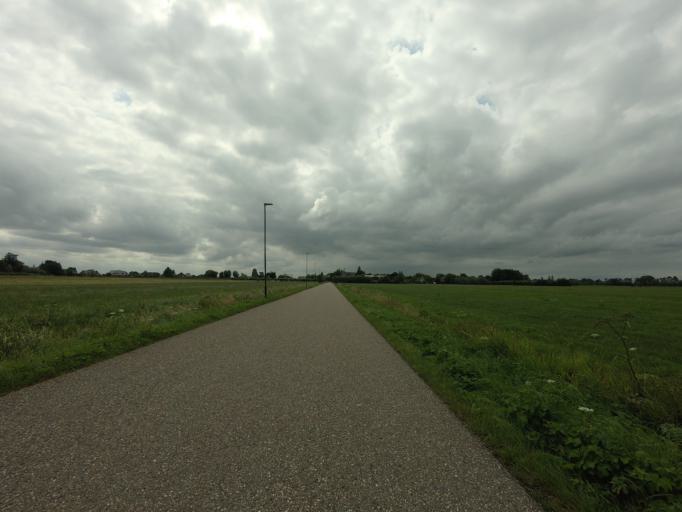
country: NL
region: South Holland
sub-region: Gemeente Giessenlanden
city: Giessenburg
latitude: 51.8639
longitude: 4.8987
